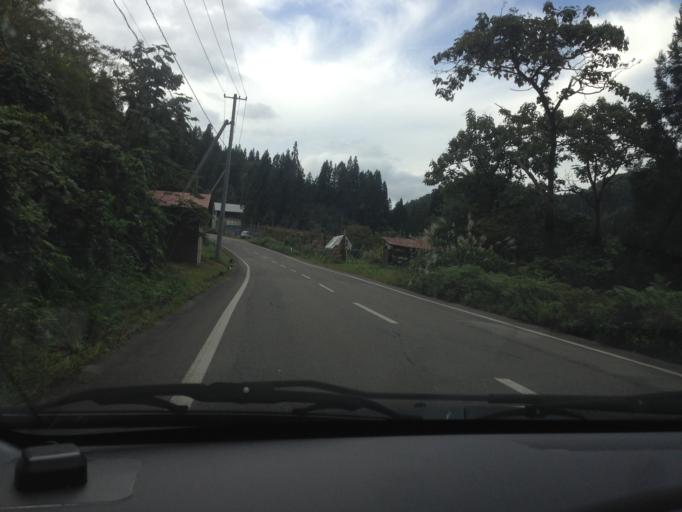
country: JP
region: Fukushima
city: Kitakata
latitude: 37.4668
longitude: 139.6957
